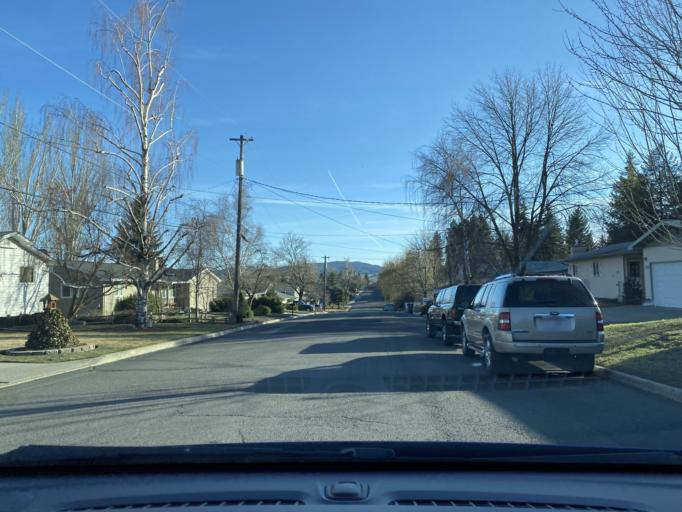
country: US
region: Idaho
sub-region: Latah County
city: Moscow
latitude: 46.7441
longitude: -116.9831
